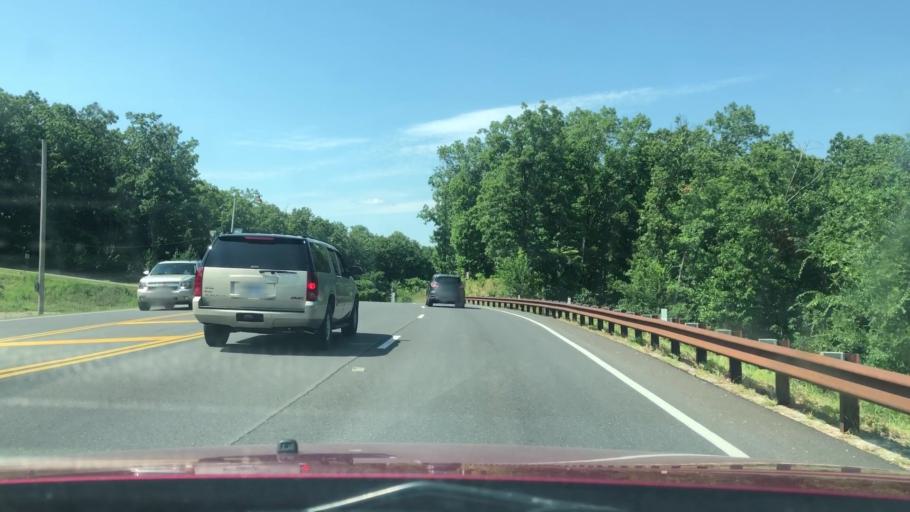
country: US
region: Missouri
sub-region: Stone County
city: Kimberling City
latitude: 36.6653
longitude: -93.3368
